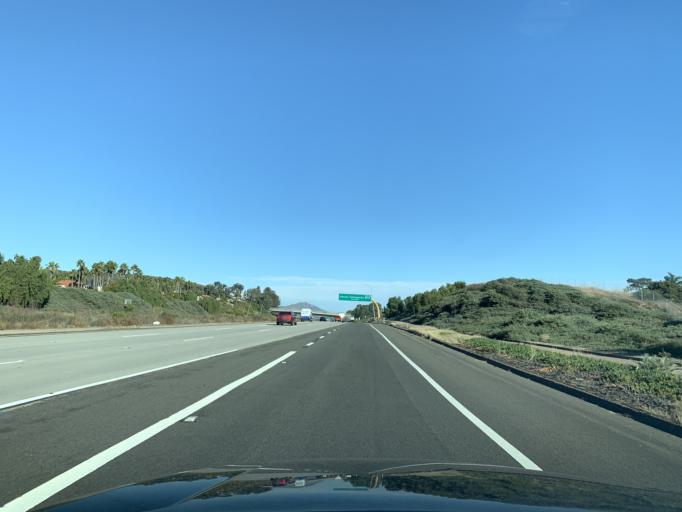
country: US
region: California
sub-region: San Diego County
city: Fairbanks Ranch
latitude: 32.9544
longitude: -117.1262
